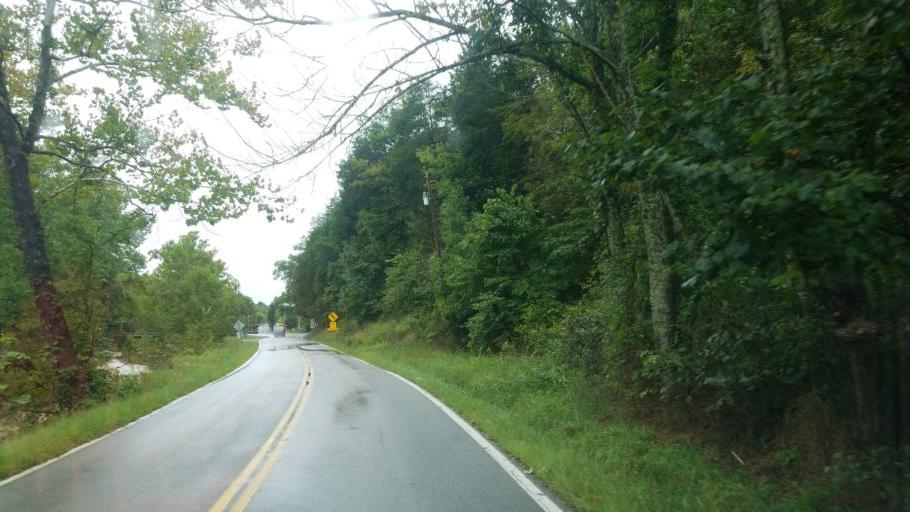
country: US
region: Ohio
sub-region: Adams County
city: West Union
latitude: 38.7477
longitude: -83.5169
